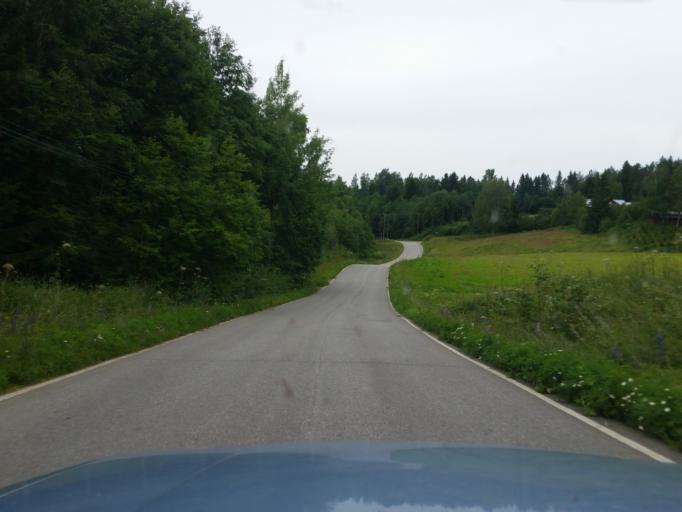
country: FI
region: Uusimaa
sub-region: Helsinki
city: Sammatti
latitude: 60.4683
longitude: 23.8436
